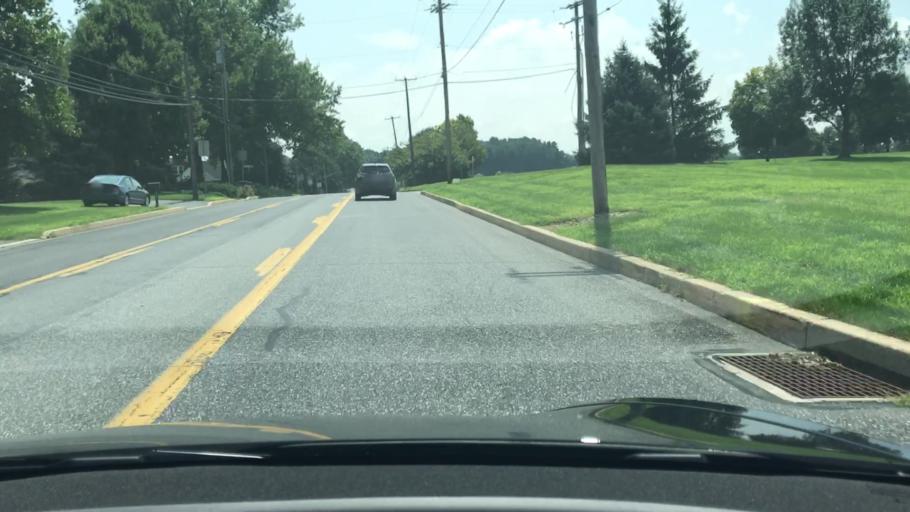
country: US
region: Pennsylvania
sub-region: Lancaster County
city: Landisville
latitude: 40.0877
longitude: -76.4094
